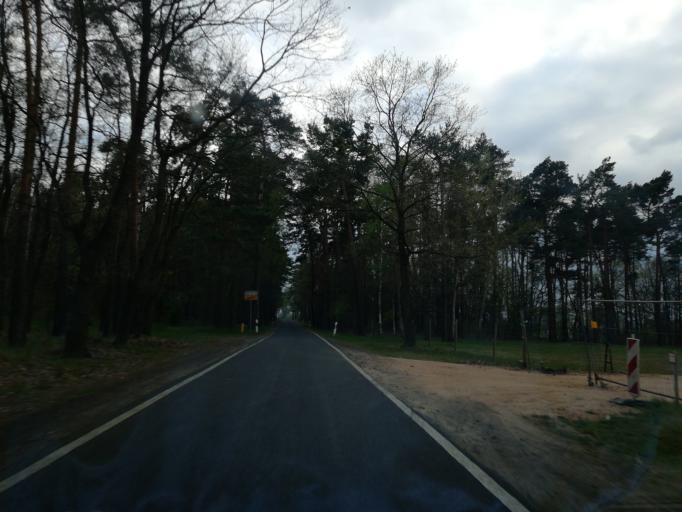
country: DE
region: Brandenburg
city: Calau
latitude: 51.7861
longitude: 13.8842
